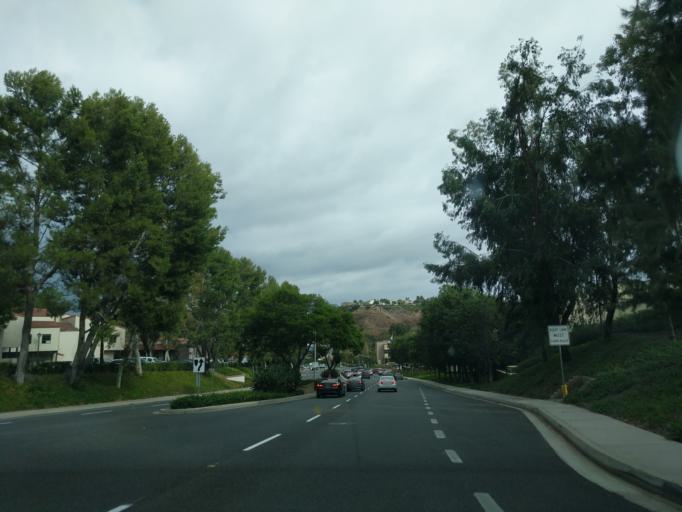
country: US
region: California
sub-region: Orange County
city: Mission Viejo
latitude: 33.5976
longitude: -117.6602
